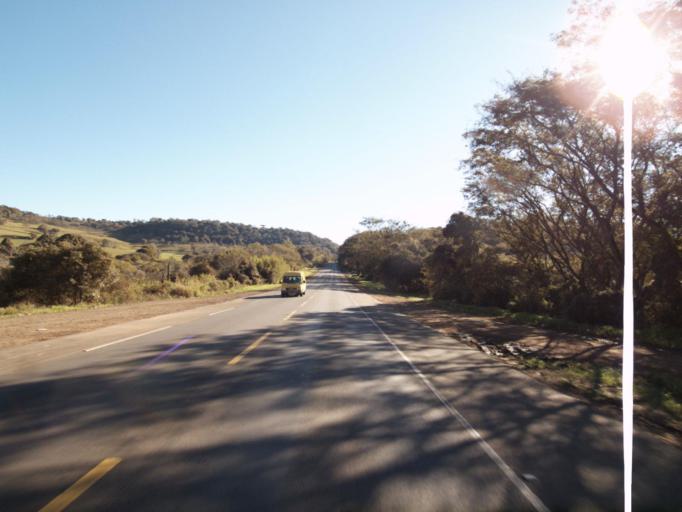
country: BR
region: Santa Catarina
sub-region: Chapeco
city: Chapeco
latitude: -26.9966
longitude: -52.6174
